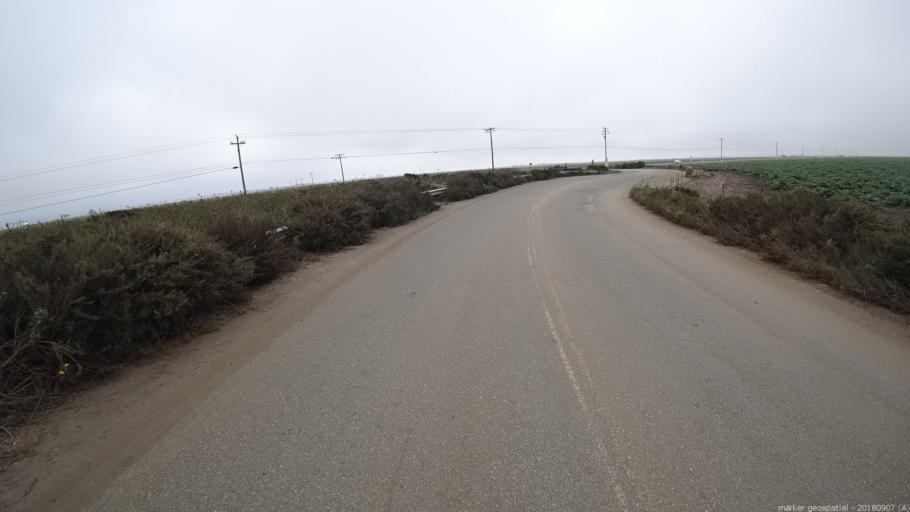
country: US
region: California
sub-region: Monterey County
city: Castroville
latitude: 36.7717
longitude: -121.7886
